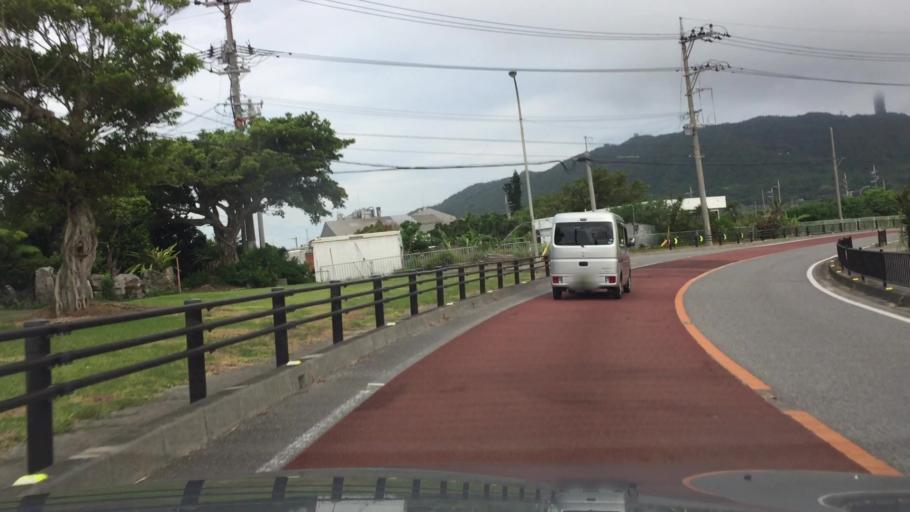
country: JP
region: Okinawa
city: Ishigaki
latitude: 24.3967
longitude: 124.1561
